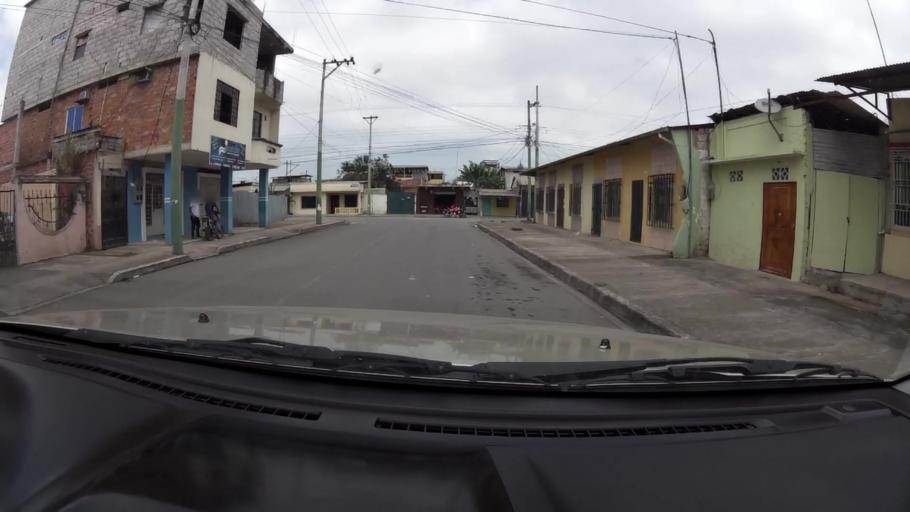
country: EC
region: El Oro
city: Pasaje
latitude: -3.2461
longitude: -79.8306
